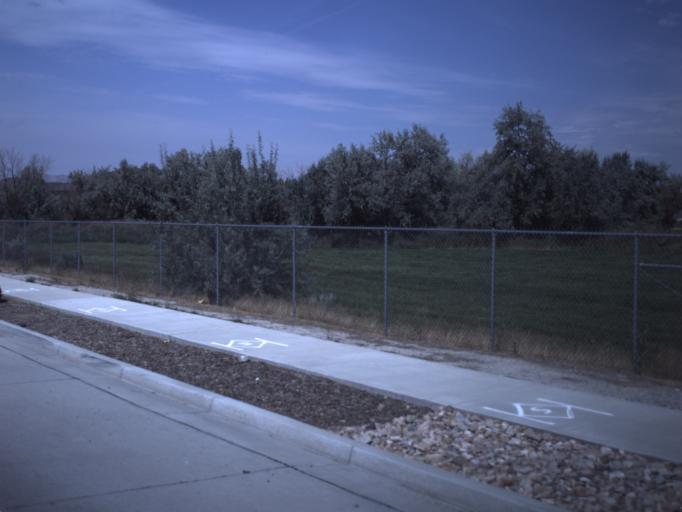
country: US
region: Utah
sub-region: Utah County
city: Lehi
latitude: 40.3735
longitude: -111.8506
